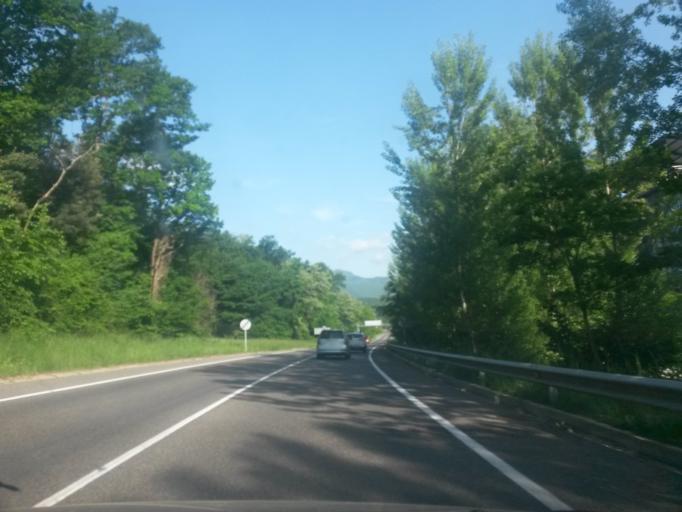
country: ES
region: Catalonia
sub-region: Provincia de Girona
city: Bas
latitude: 42.1255
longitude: 2.4535
